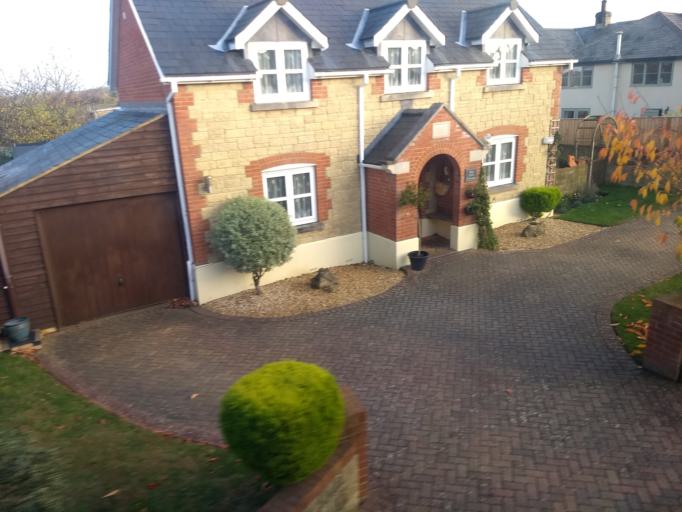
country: GB
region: England
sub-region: Isle of Wight
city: Shalfleet
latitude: 50.6865
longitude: -1.4193
